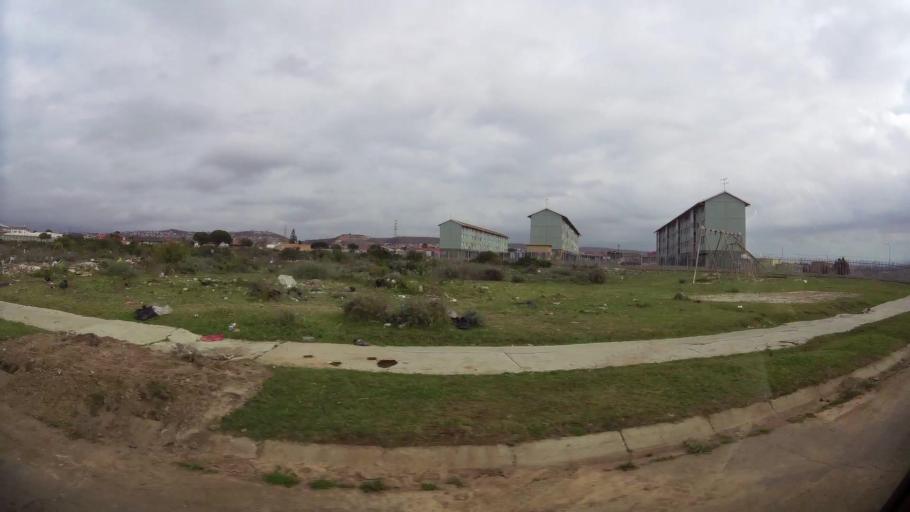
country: ZA
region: Eastern Cape
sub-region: Nelson Mandela Bay Metropolitan Municipality
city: Port Elizabeth
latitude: -33.8949
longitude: 25.5550
